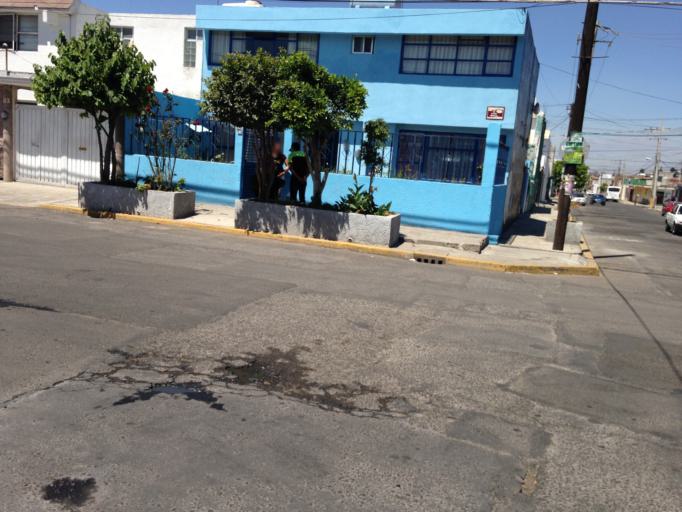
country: MX
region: Puebla
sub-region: San Pedro Cholula
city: Santiago Momoxpan
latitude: 19.0662
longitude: -98.2316
